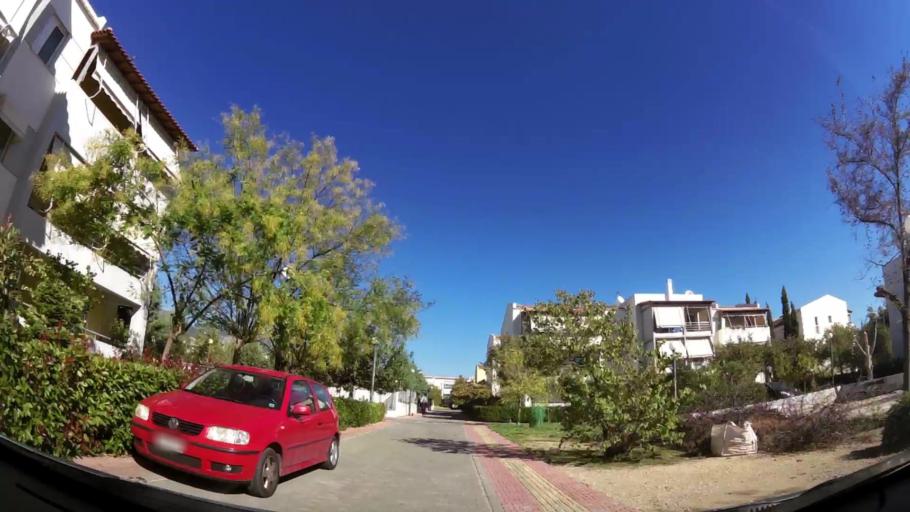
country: GR
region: Attica
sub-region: Nomarchia Anatolikis Attikis
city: Varybobi
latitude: 38.1084
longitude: 23.7708
